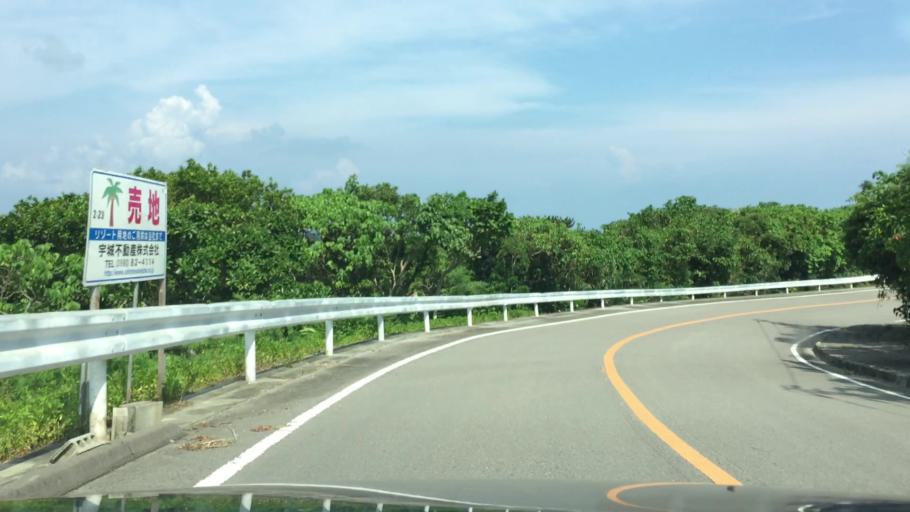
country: JP
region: Okinawa
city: Ishigaki
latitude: 24.5142
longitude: 124.2649
